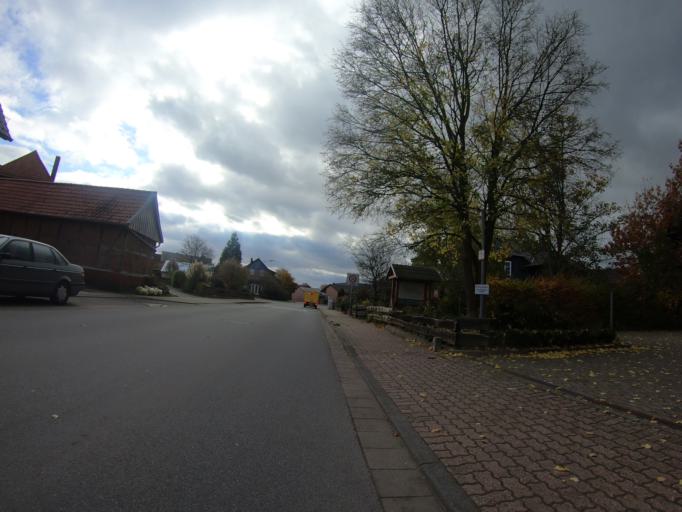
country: DE
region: Lower Saxony
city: Ribbesbuttel
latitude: 52.4260
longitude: 10.4842
